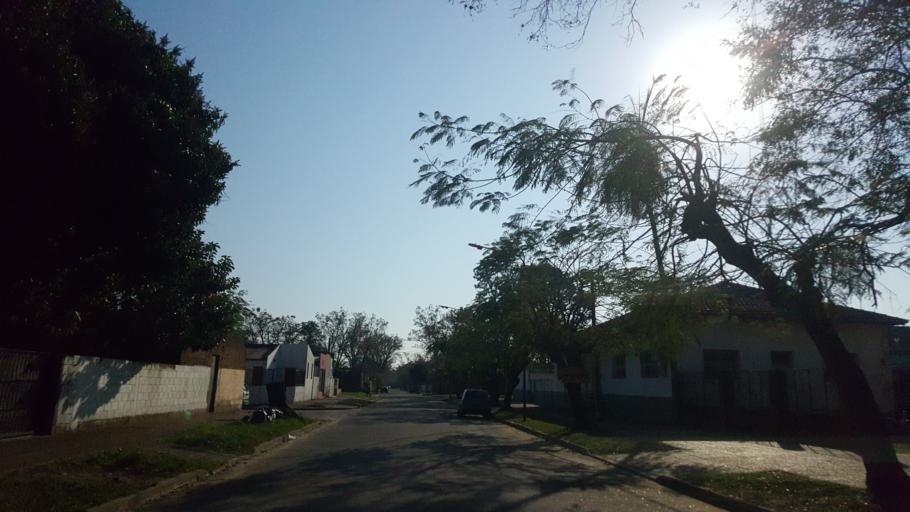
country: AR
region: Corrientes
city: Ituzaingo
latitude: -27.5817
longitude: -56.6826
